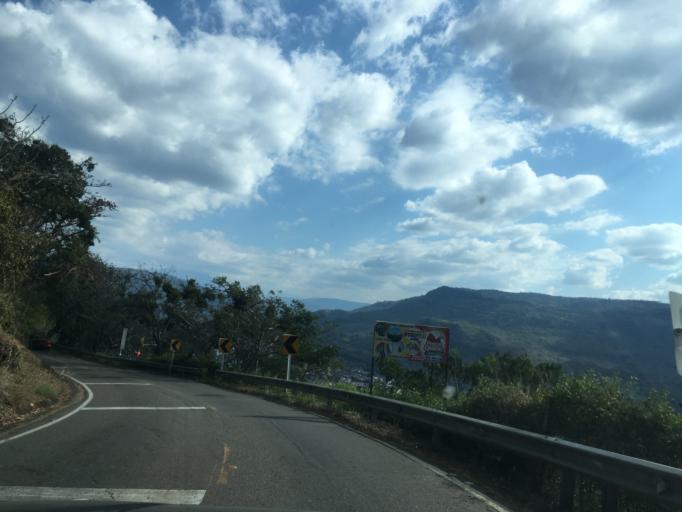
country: CO
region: Santander
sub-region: San Gil
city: San Gil
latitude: 6.5709
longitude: -73.1496
